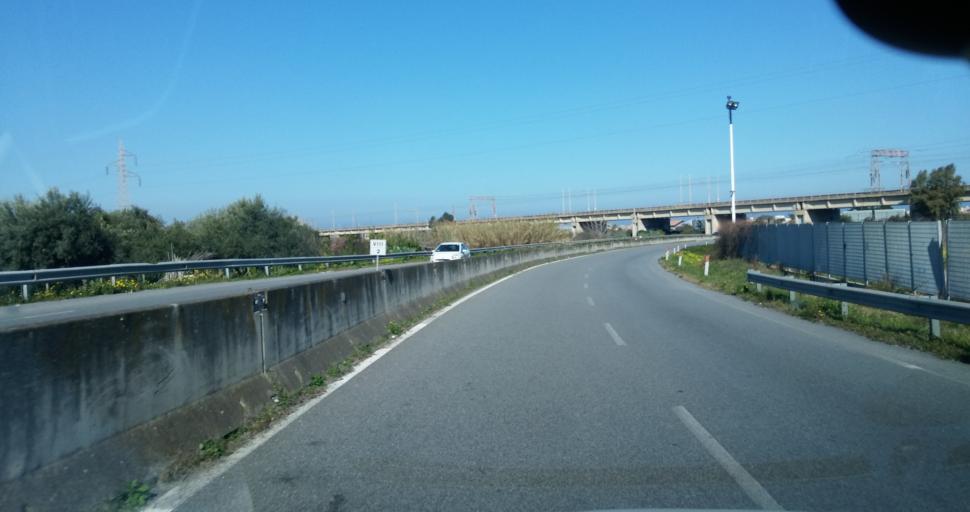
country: IT
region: Sicily
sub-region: Messina
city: Milazzo
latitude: 38.1977
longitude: 15.2485
